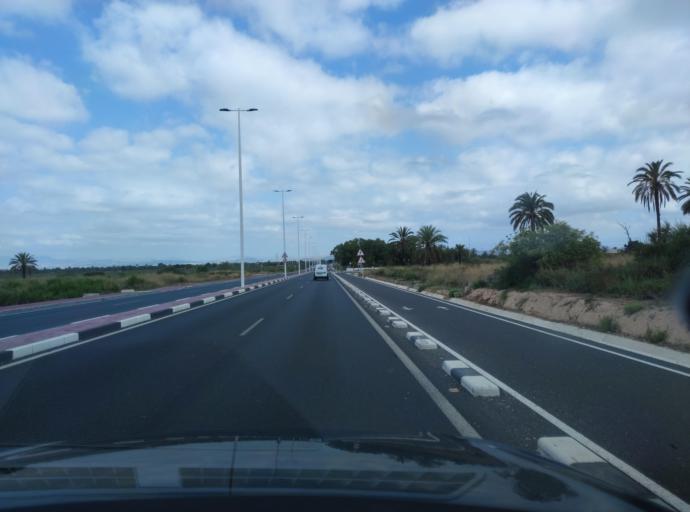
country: ES
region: Valencia
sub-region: Provincia de Alicante
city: Santa Pola
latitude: 38.2118
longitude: -0.5894
